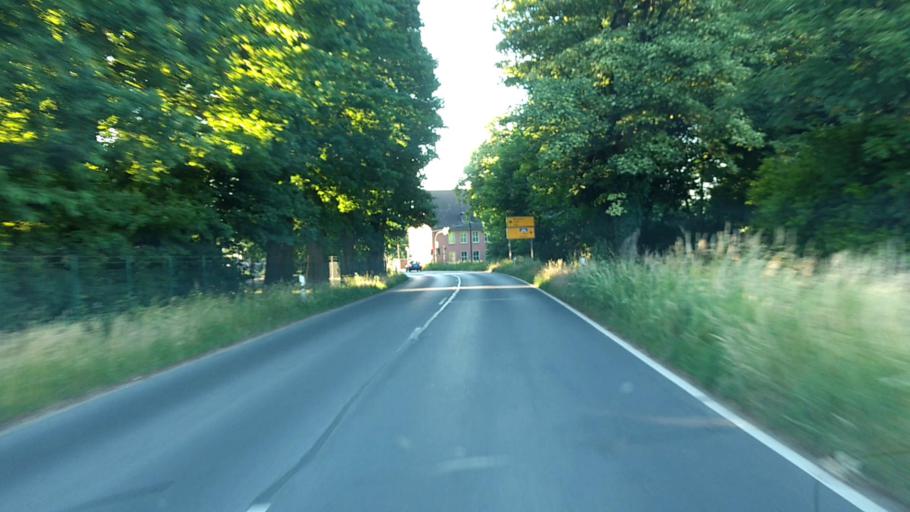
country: DE
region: North Rhine-Westphalia
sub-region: Regierungsbezirk Koln
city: Bergheim
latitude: 50.9162
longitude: 6.6670
